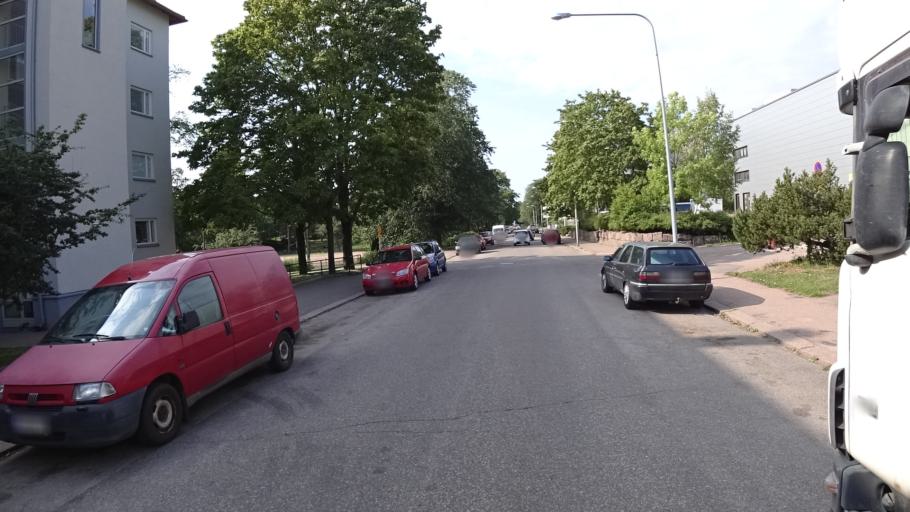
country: FI
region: Kymenlaakso
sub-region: Kotka-Hamina
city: Kotka
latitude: 60.4649
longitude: 26.9523
